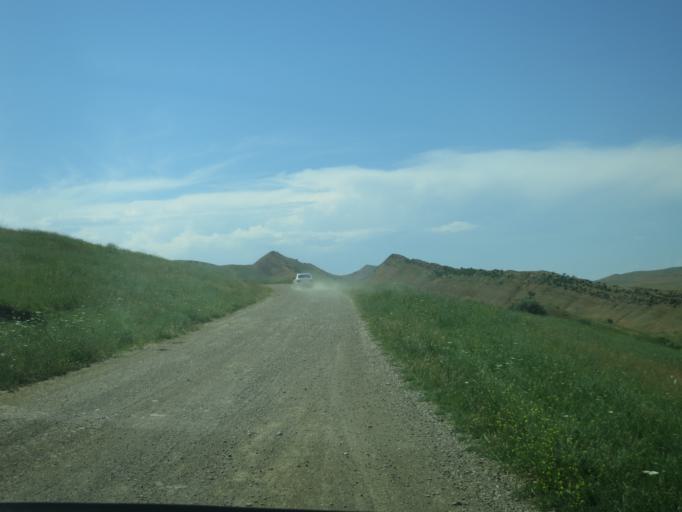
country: AZ
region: Agstafa
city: Saloglu
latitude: 41.4582
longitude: 45.3589
